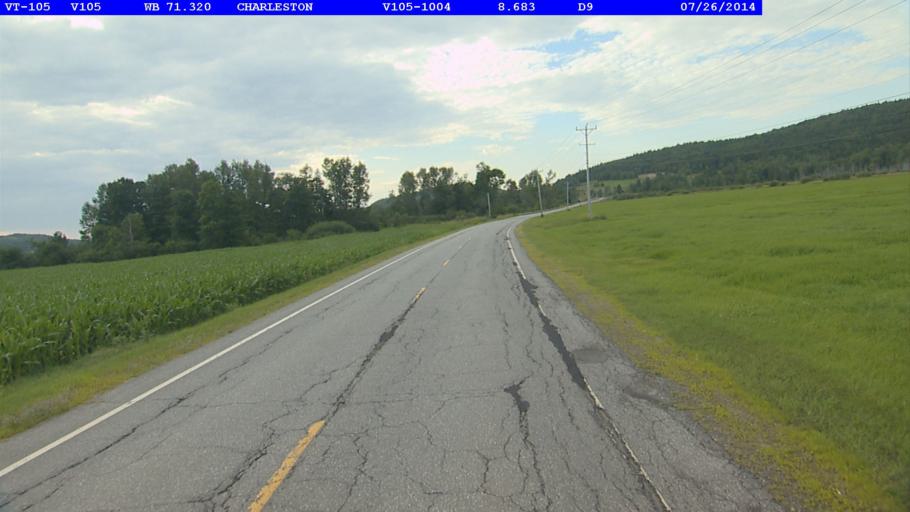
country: US
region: Vermont
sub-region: Orleans County
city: Newport
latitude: 44.8211
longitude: -71.9708
